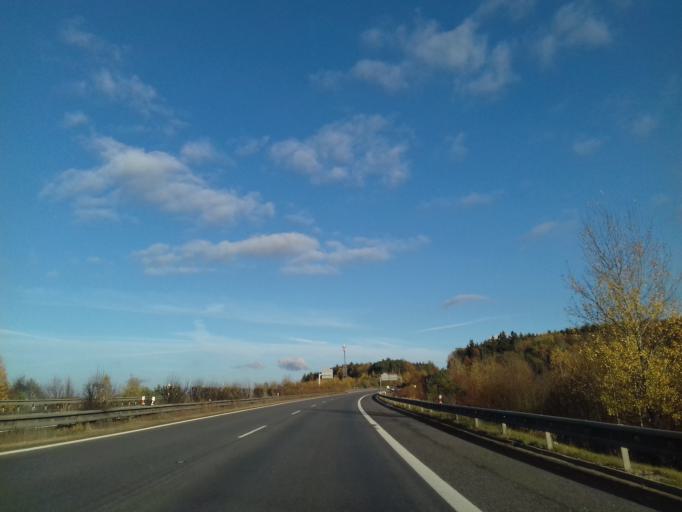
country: CZ
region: Plzensky
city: Dysina
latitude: 49.7368
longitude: 13.5122
